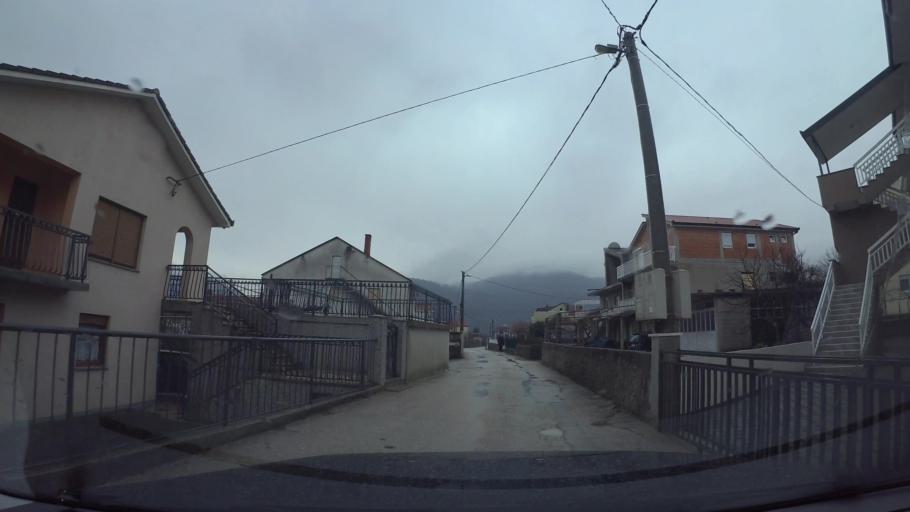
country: BA
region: Federation of Bosnia and Herzegovina
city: Cim
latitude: 43.3512
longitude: 17.7865
